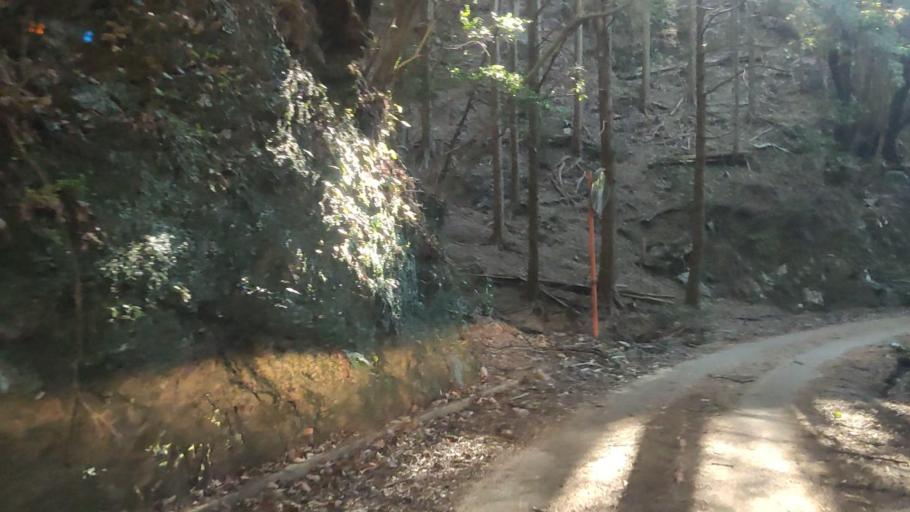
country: JP
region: Oita
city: Saiki
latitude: 32.7862
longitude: 131.8528
